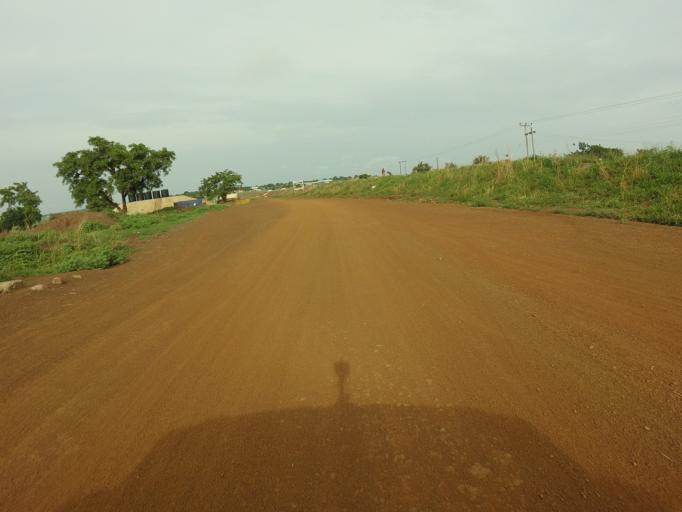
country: GH
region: Northern
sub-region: Yendi
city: Yendi
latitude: 9.9314
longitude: -0.2040
